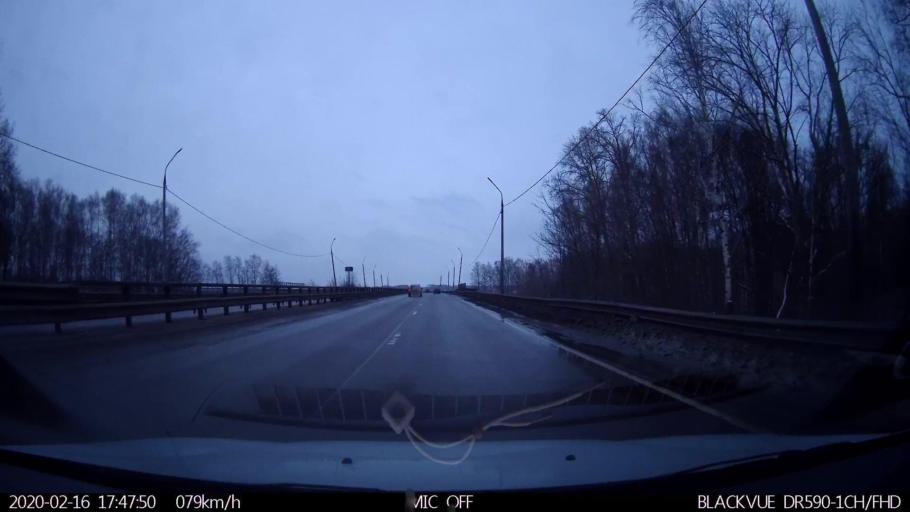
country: RU
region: Nizjnij Novgorod
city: Afonino
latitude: 56.2184
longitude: 44.0772
